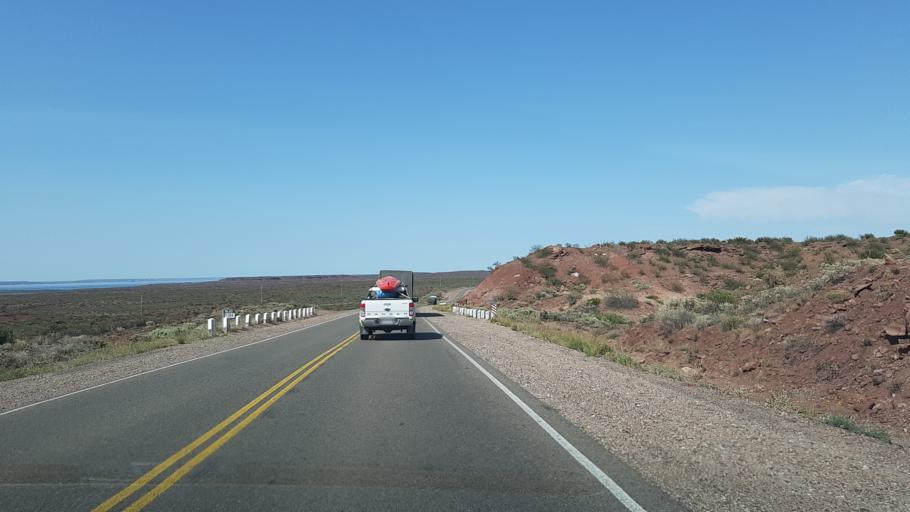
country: AR
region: Neuquen
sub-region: Departamento de Picun Leufu
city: Picun Leufu
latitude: -39.2778
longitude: -68.8577
